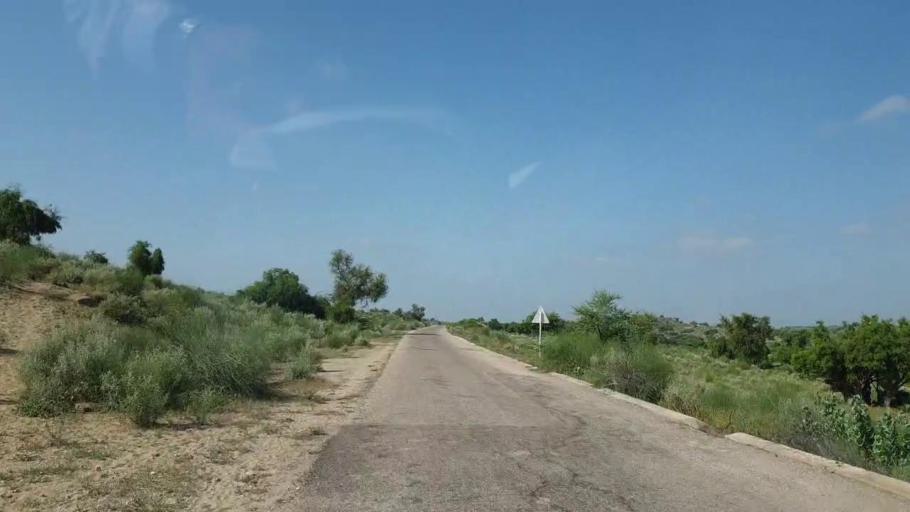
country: PK
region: Sindh
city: Mithi
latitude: 24.5673
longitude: 69.9162
